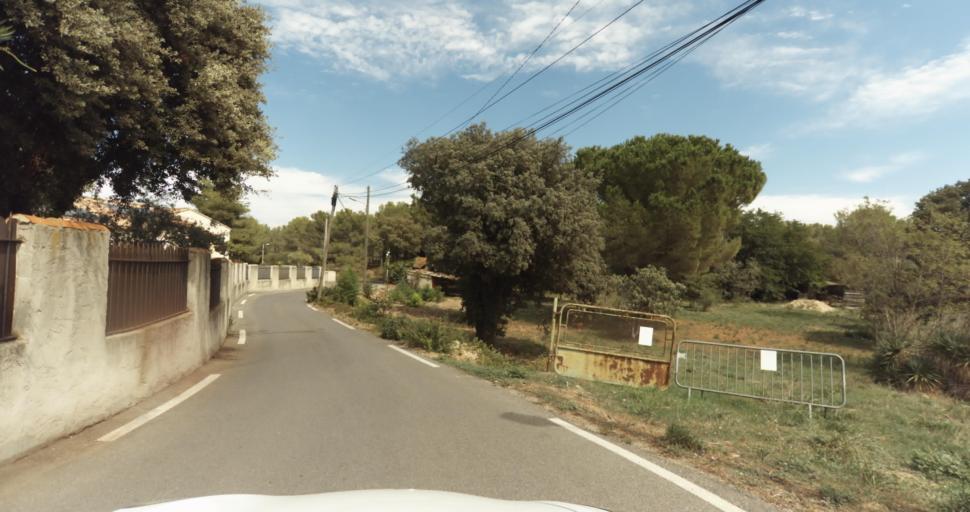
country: FR
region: Provence-Alpes-Cote d'Azur
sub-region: Departement des Bouches-du-Rhone
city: Miramas
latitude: 43.5840
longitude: 5.0212
